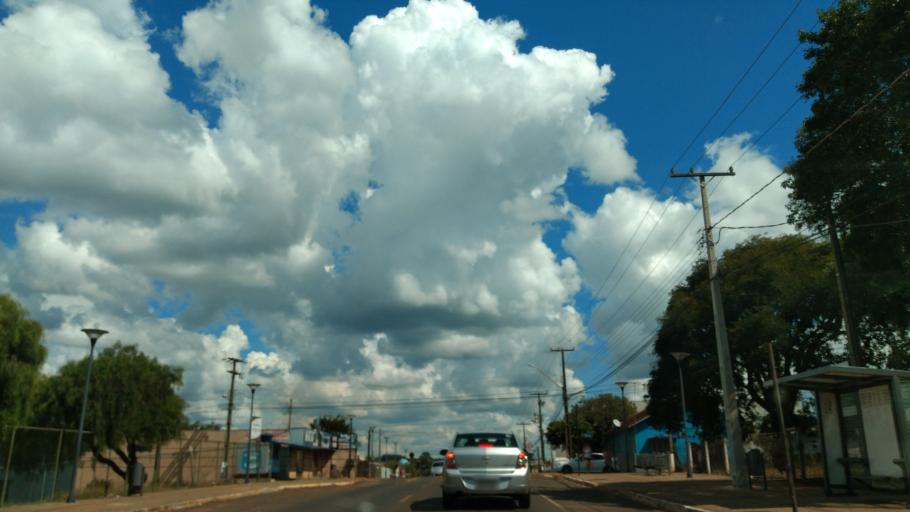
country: BR
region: Parana
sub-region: Guarapuava
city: Guarapuava
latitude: -25.4012
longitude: -51.4932
